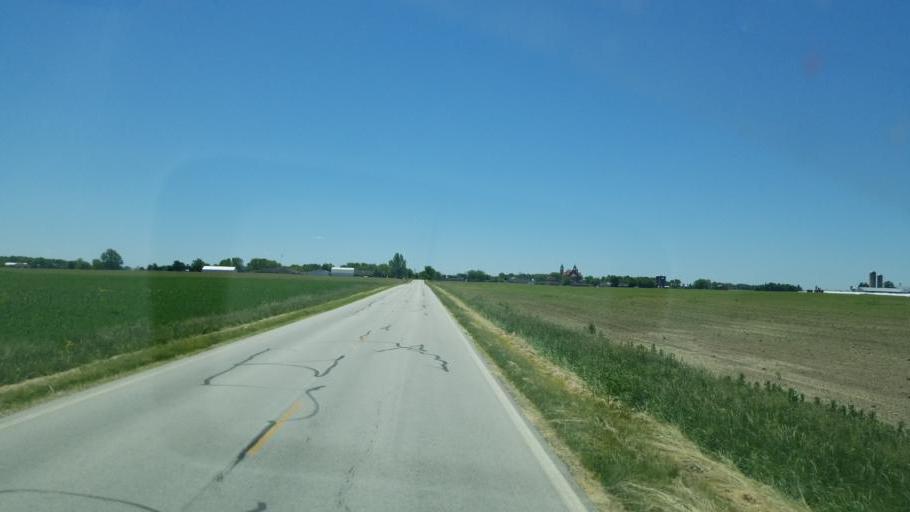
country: US
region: Ohio
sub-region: Mercer County
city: Saint Henry
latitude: 40.3615
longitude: -84.6433
